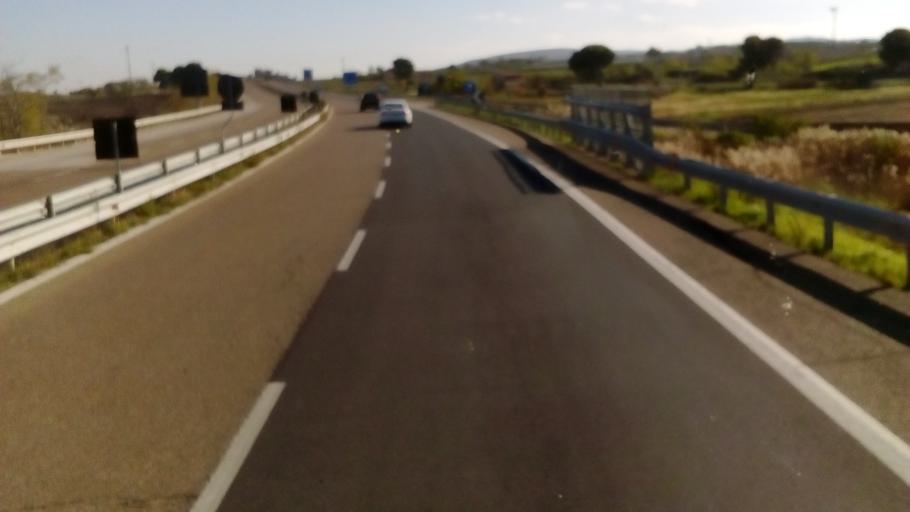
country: IT
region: Basilicate
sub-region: Provincia di Potenza
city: Zona 179
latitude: 41.0880
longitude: 15.5974
